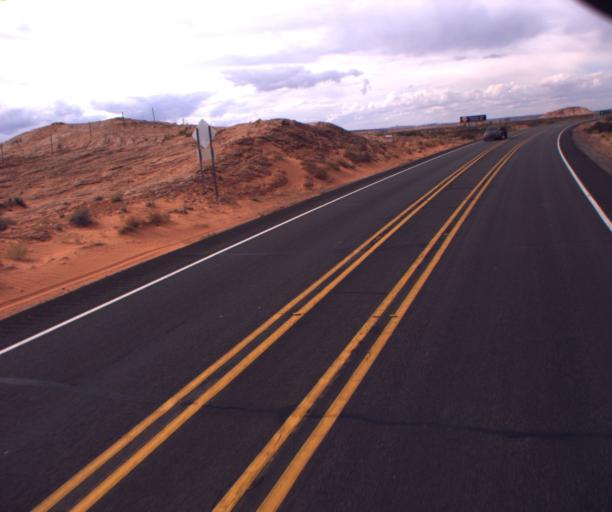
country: US
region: Arizona
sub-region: Apache County
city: Many Farms
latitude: 36.9246
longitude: -109.6126
